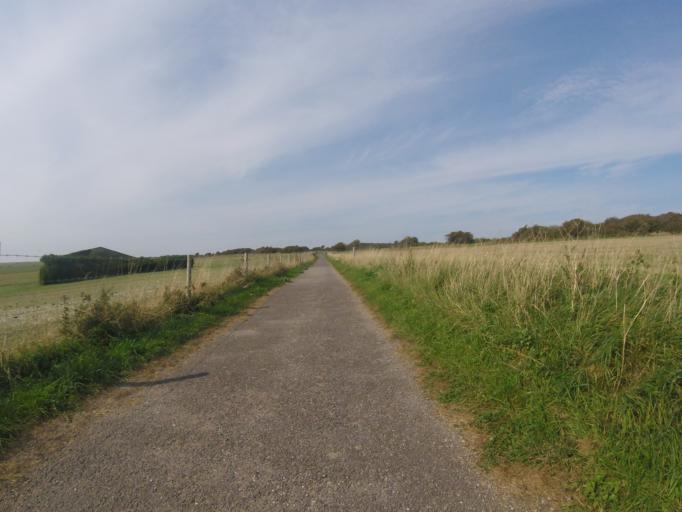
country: GB
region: England
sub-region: West Sussex
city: Fulking
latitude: 50.8735
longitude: -0.2003
